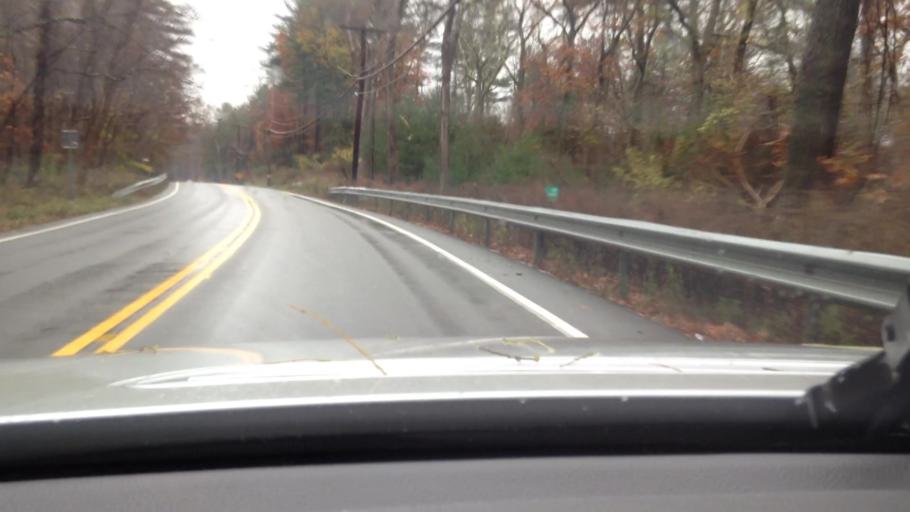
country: US
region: New York
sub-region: Orange County
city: West Point
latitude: 41.3997
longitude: -73.9331
